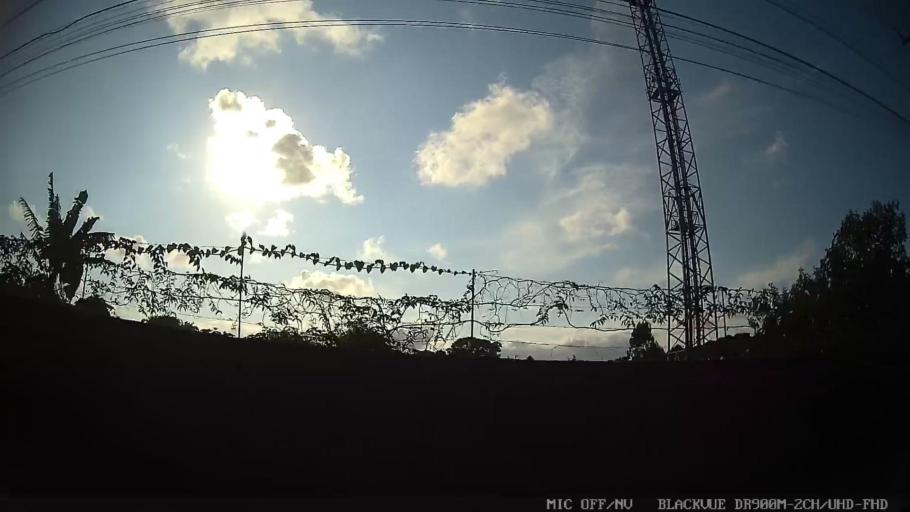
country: BR
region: Sao Paulo
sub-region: Itanhaem
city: Itanhaem
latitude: -24.1788
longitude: -46.8245
